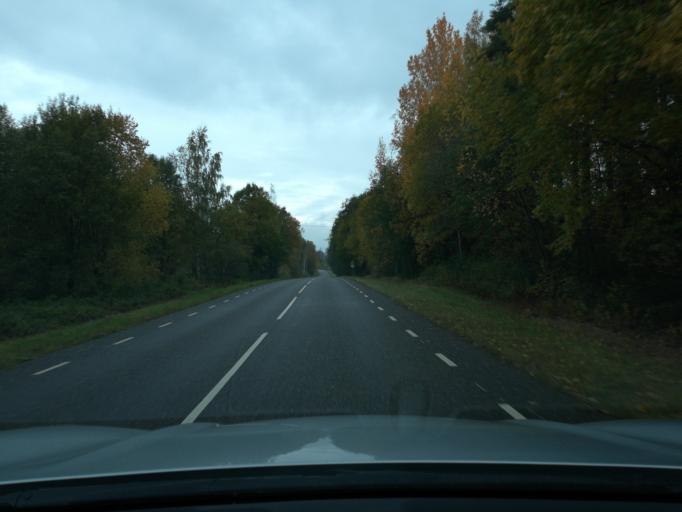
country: EE
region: Ida-Virumaa
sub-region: Johvi vald
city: Johvi
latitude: 59.0649
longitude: 27.3820
